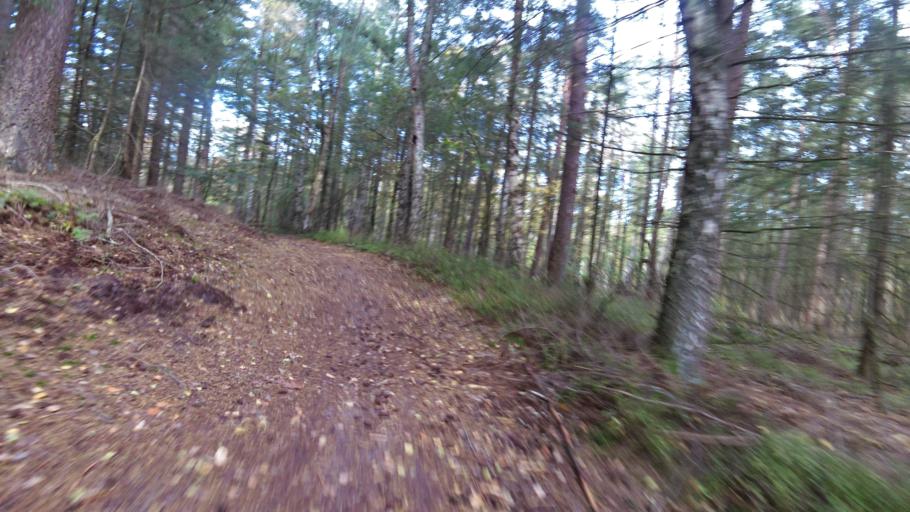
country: NL
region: Gelderland
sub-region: Gemeente Epe
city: Emst
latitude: 52.3368
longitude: 5.9209
